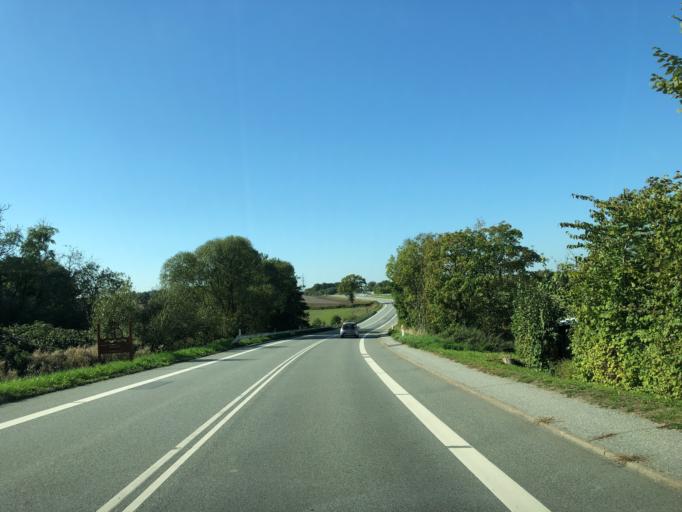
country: DK
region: South Denmark
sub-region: Aabenraa Kommune
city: Aabenraa
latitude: 55.0157
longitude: 9.4469
